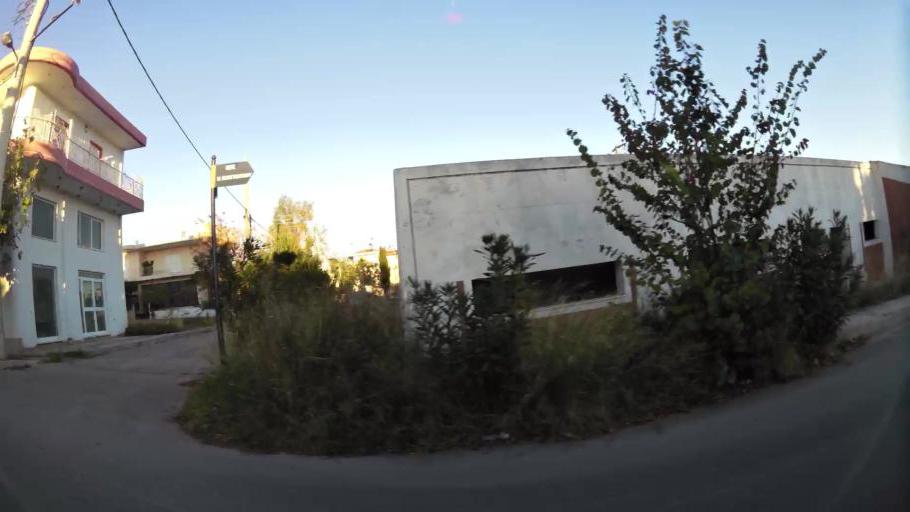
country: GR
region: Attica
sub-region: Nomarchia Dytikis Attikis
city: Ano Liosia
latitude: 38.0869
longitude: 23.6900
